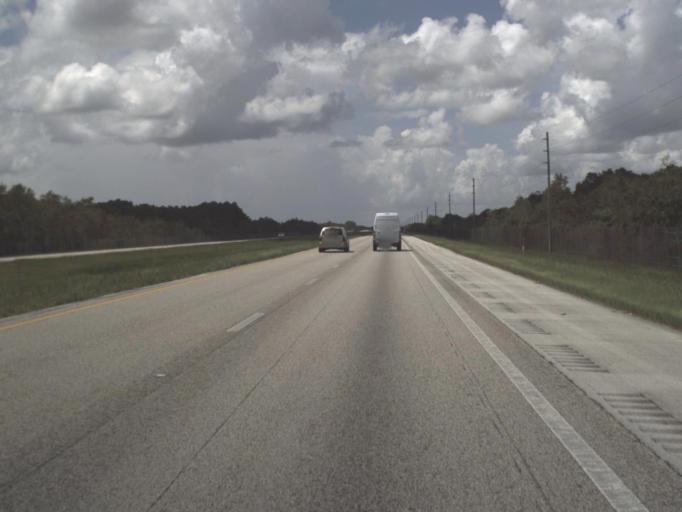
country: US
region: Florida
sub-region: Broward County
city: Weston
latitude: 26.1719
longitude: -80.9258
